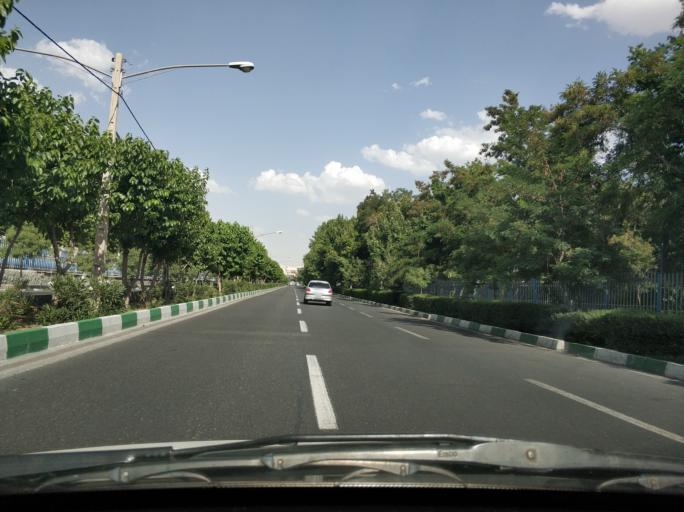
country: IR
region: Tehran
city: Tajrish
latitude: 35.7438
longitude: 51.5801
